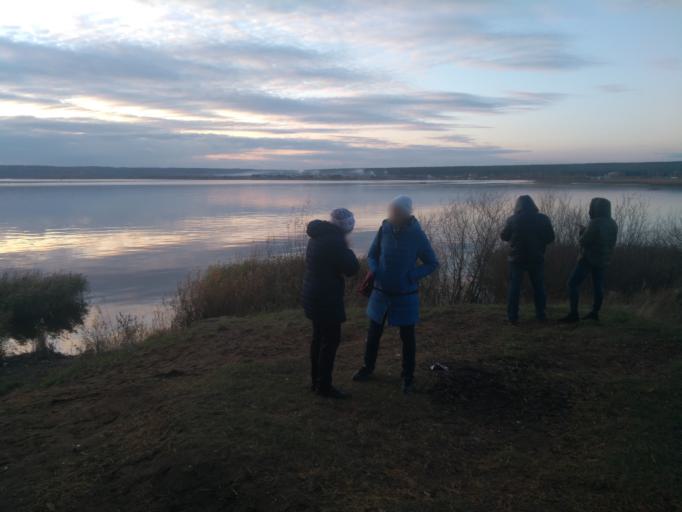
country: RU
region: Tatarstan
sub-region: Tukayevskiy Rayon
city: Naberezhnyye Chelny
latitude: 55.7679
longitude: 52.4019
